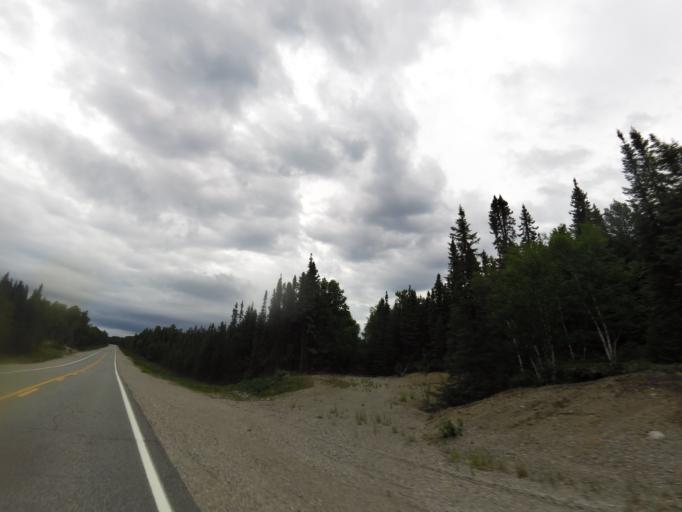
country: CA
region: Quebec
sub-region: Abitibi-Temiscamingue
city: Amos
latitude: 48.9612
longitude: -77.9542
